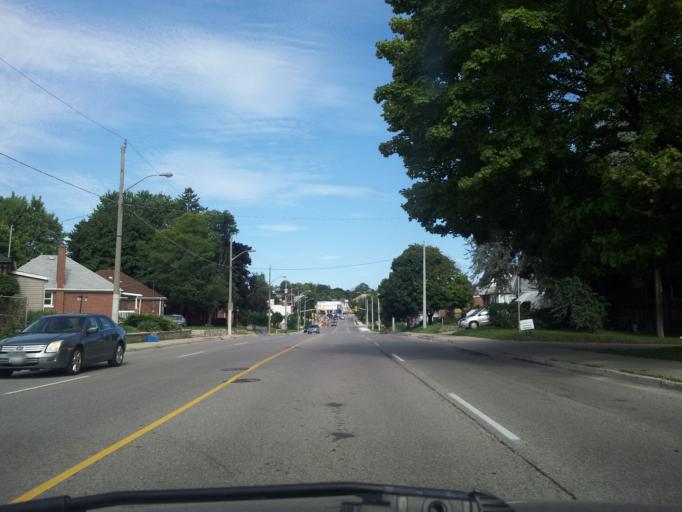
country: CA
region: Ontario
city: Kitchener
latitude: 43.4428
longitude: -80.4807
